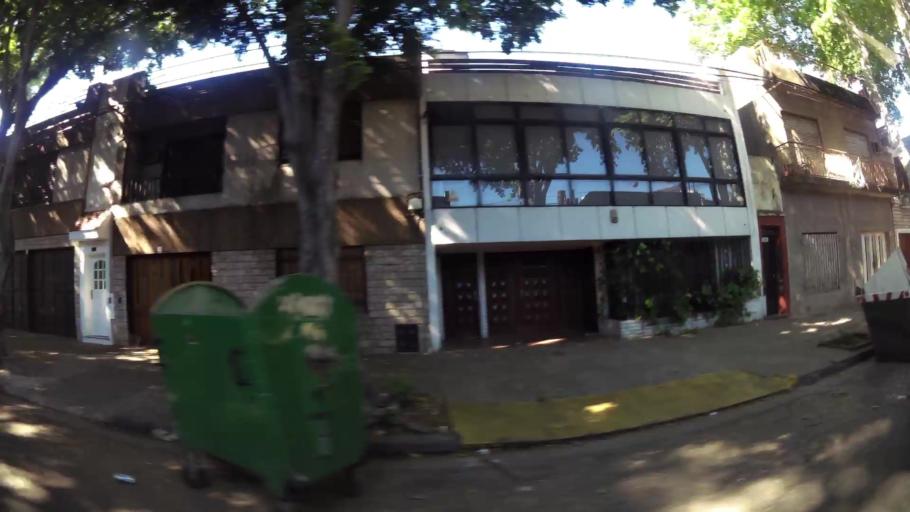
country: AR
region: Santa Fe
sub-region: Departamento de Rosario
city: Rosario
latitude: -32.9474
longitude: -60.6762
